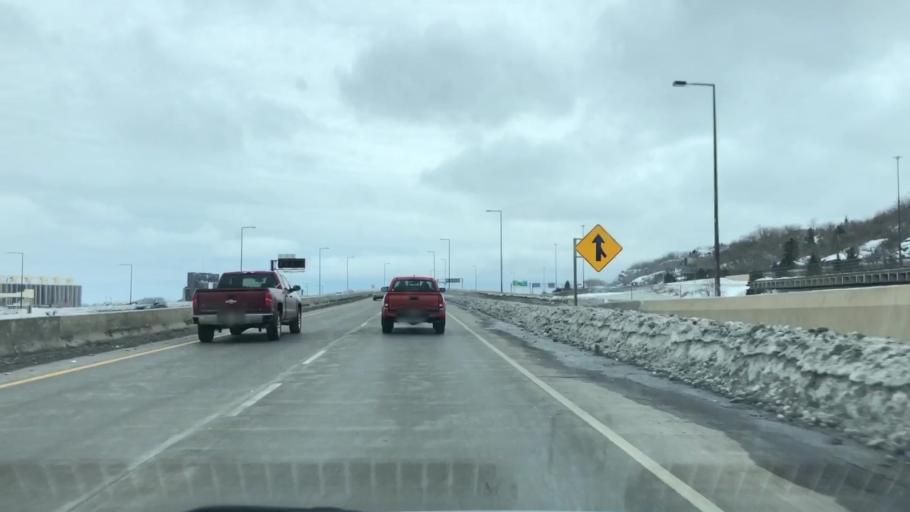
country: US
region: Minnesota
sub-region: Saint Louis County
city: Duluth
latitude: 46.7802
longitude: -92.1041
